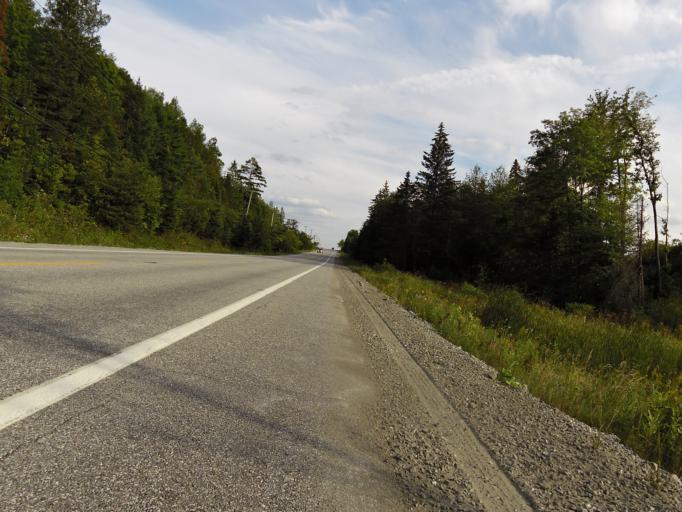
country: CA
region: Quebec
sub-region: Outaouais
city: Wakefield
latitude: 45.6089
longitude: -75.9099
